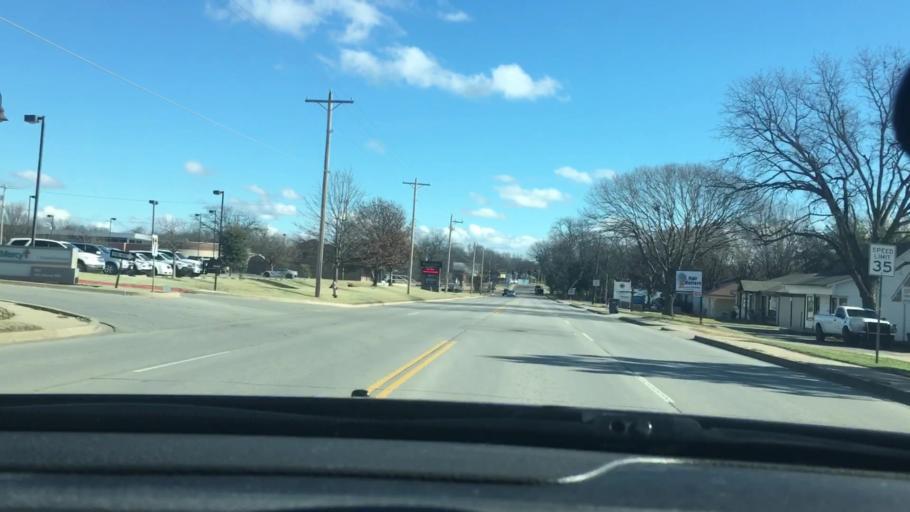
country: US
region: Oklahoma
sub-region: Carter County
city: Ardmore
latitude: 34.1870
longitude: -97.1408
